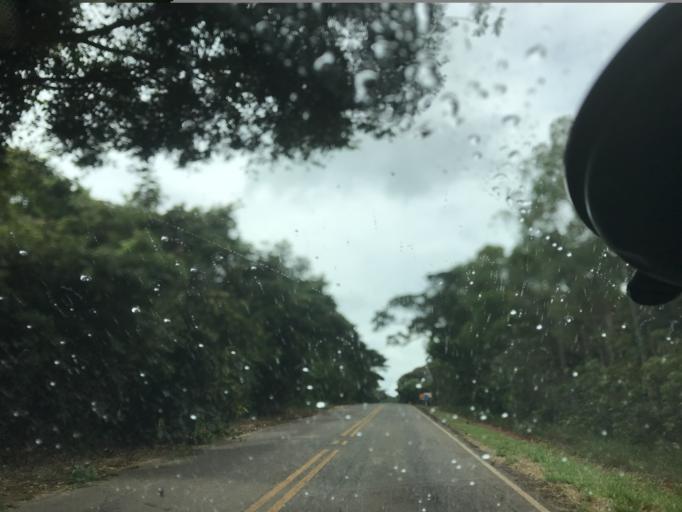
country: BR
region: Minas Gerais
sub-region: Conceicao Do Rio Verde
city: Conceicao do Rio Verde
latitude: -21.6832
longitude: -45.0165
